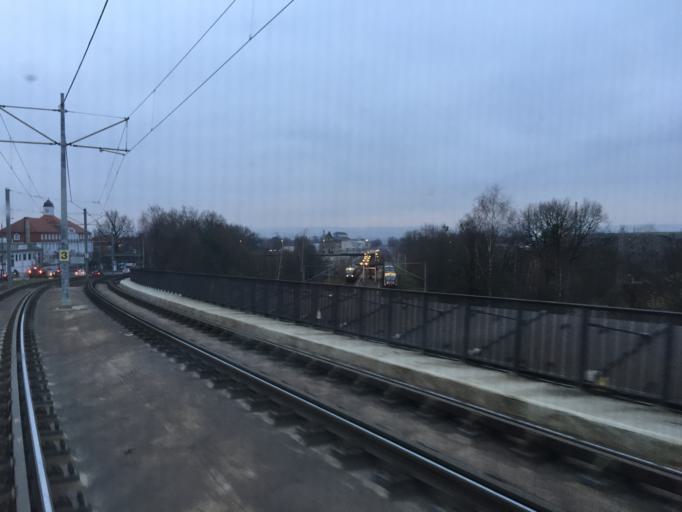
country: DE
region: Saxony
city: Albertstadt
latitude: 51.0889
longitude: 13.7640
